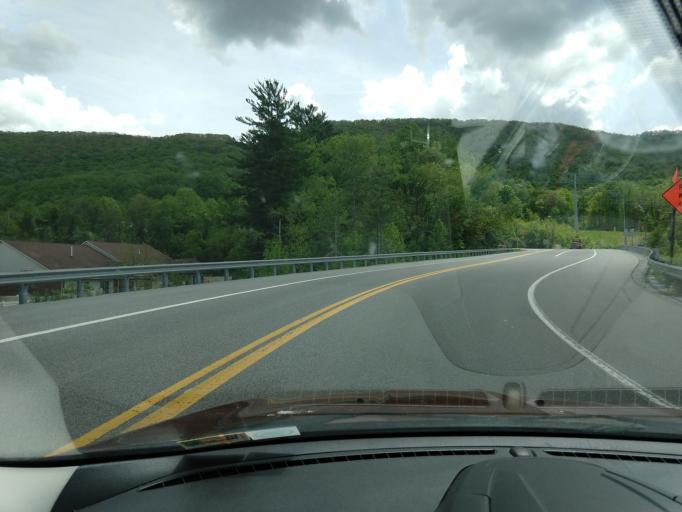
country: US
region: West Virginia
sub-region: Mercer County
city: Bluefield
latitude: 37.2455
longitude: -81.2267
